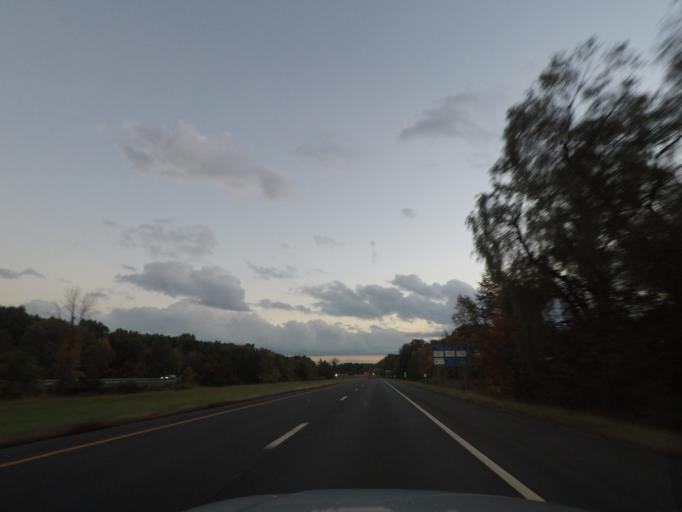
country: US
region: New York
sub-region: Ulster County
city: New Paltz
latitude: 41.7508
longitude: -74.0616
